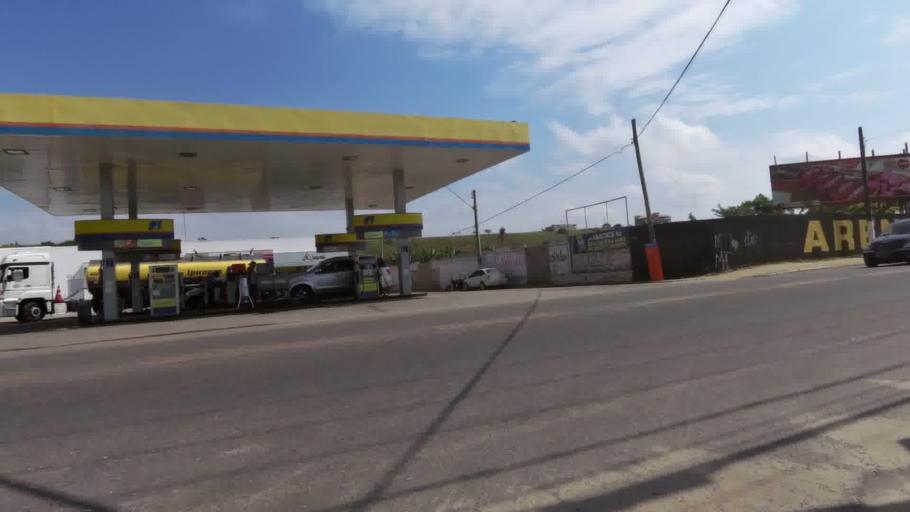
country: BR
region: Espirito Santo
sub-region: Marataizes
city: Marataizes
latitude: -21.0278
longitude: -40.8170
